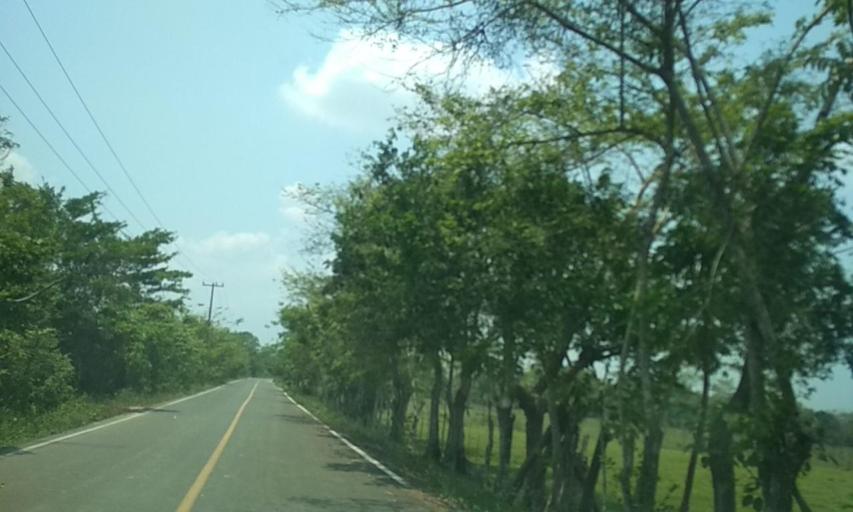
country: MX
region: Tabasco
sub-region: Huimanguillo
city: Francisco Rueda
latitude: 17.7602
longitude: -94.0122
